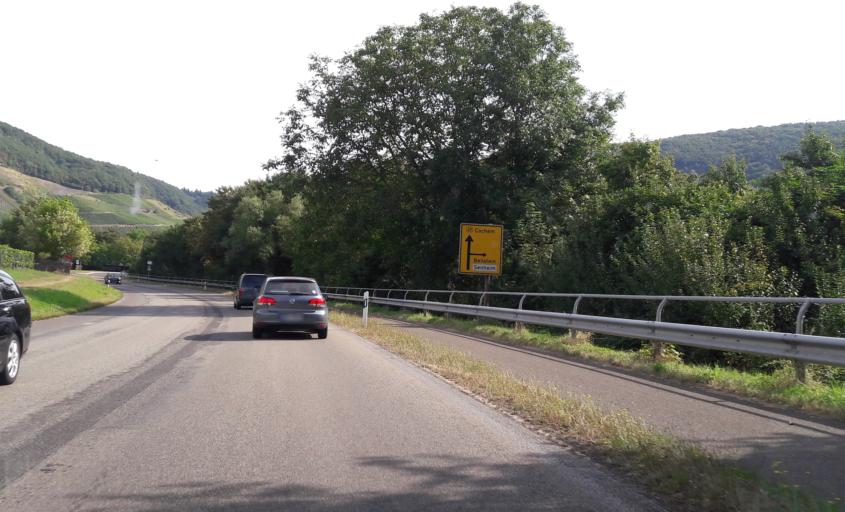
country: DE
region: Rheinland-Pfalz
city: Nehren
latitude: 50.0818
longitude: 7.1988
